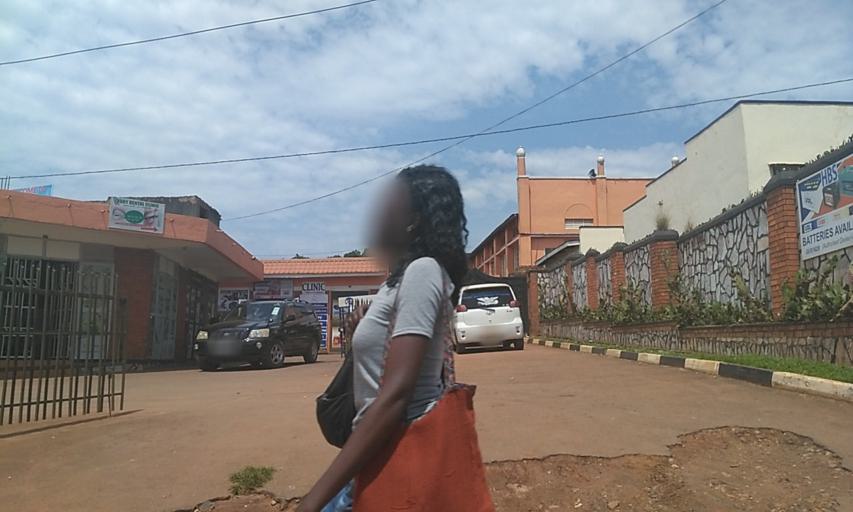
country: UG
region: Central Region
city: Kampala Central Division
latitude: 0.3108
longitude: 32.5651
